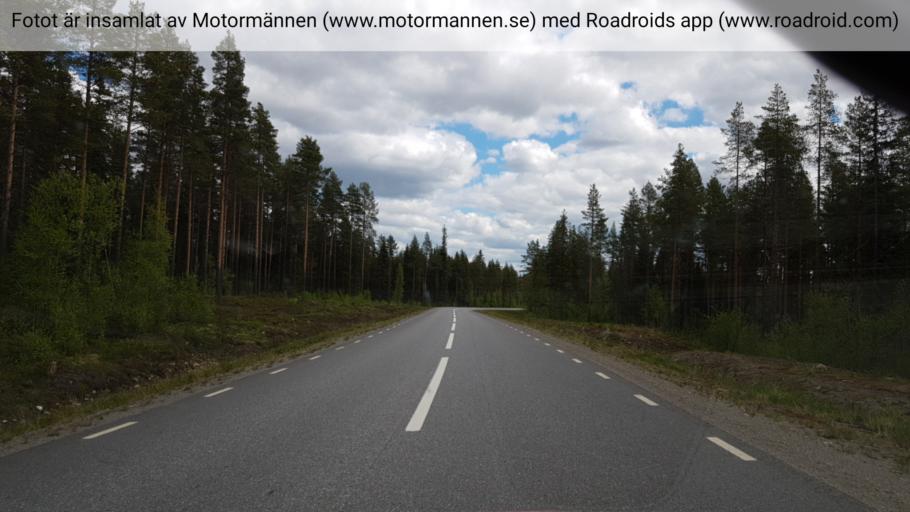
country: SE
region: Vaesterbotten
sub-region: Skelleftea Kommun
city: Langsele
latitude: 64.8377
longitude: 19.8891
